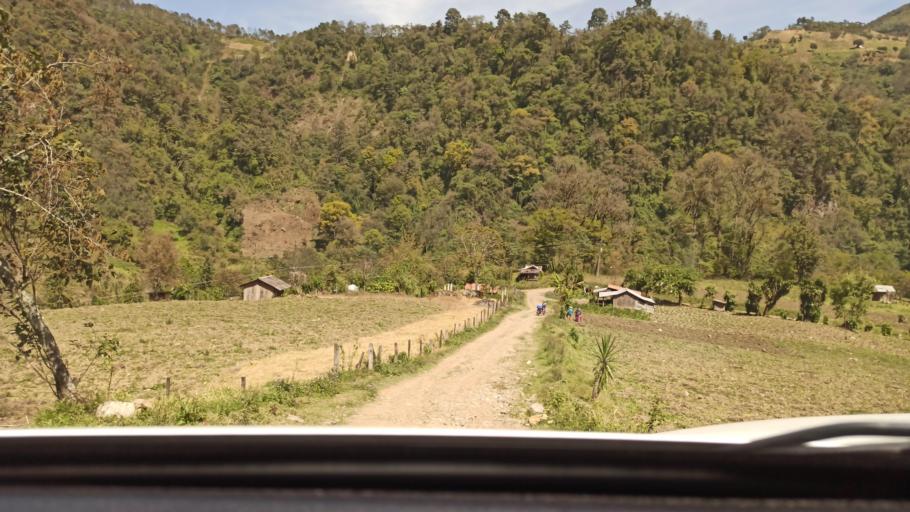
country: MX
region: Veracruz
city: Xocotla
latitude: 18.9898
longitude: -97.0990
